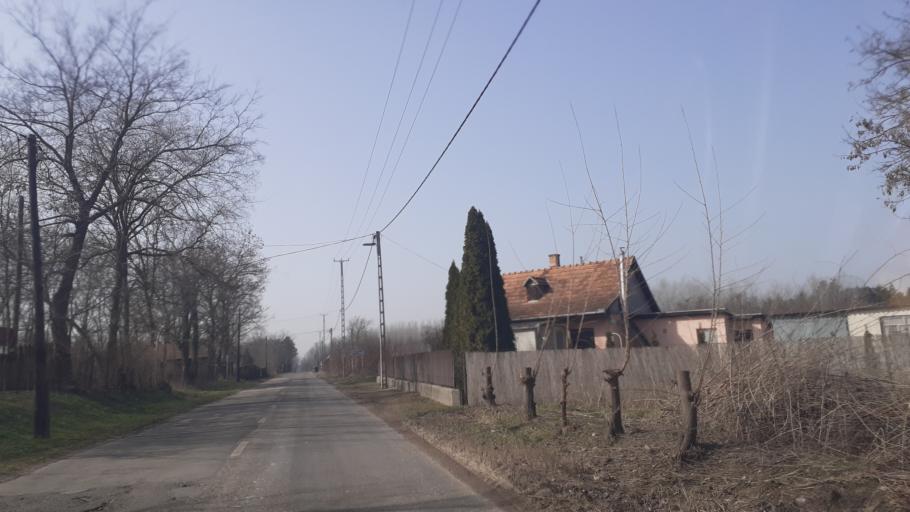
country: HU
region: Bacs-Kiskun
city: Kunszentmiklos
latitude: 47.0212
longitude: 19.2080
